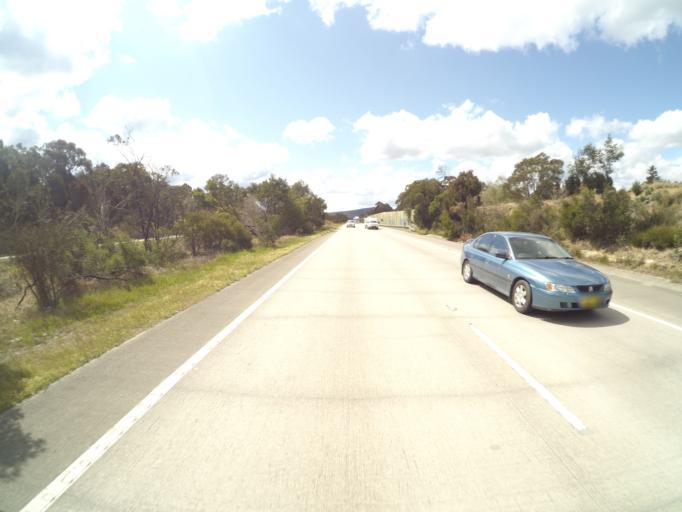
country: AU
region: New South Wales
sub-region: Wingecarribee
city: Mittagong
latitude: -34.4388
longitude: 150.4192
